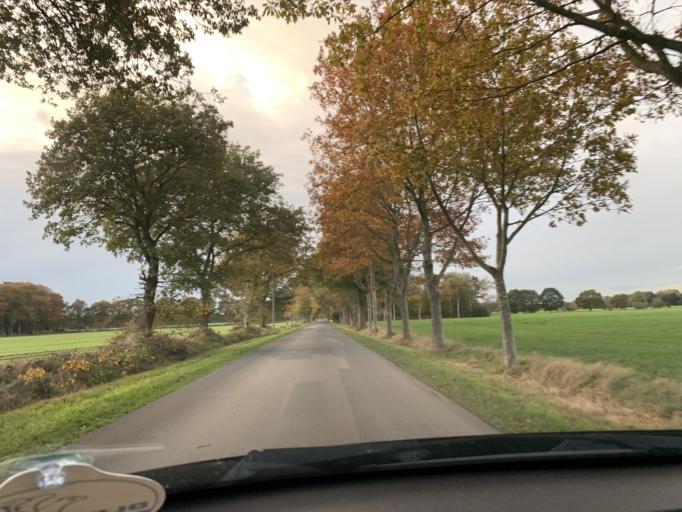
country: DE
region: Lower Saxony
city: Wiefelstede
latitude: 53.2630
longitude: 8.0958
